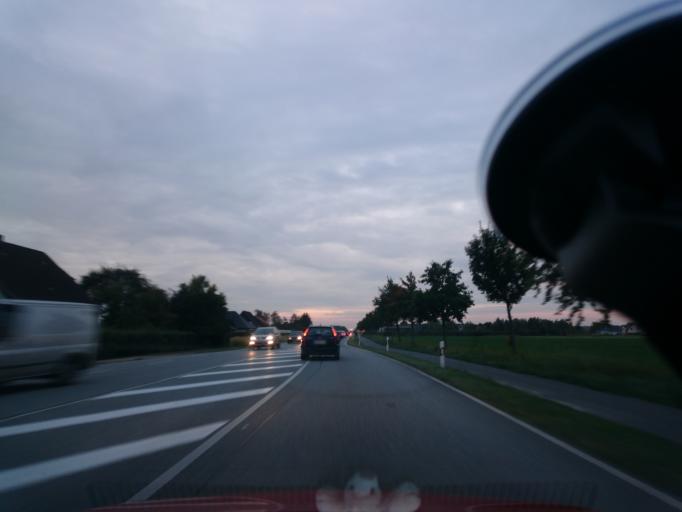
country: DE
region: Mecklenburg-Vorpommern
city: Monchhagen
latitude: 54.1520
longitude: 12.2293
